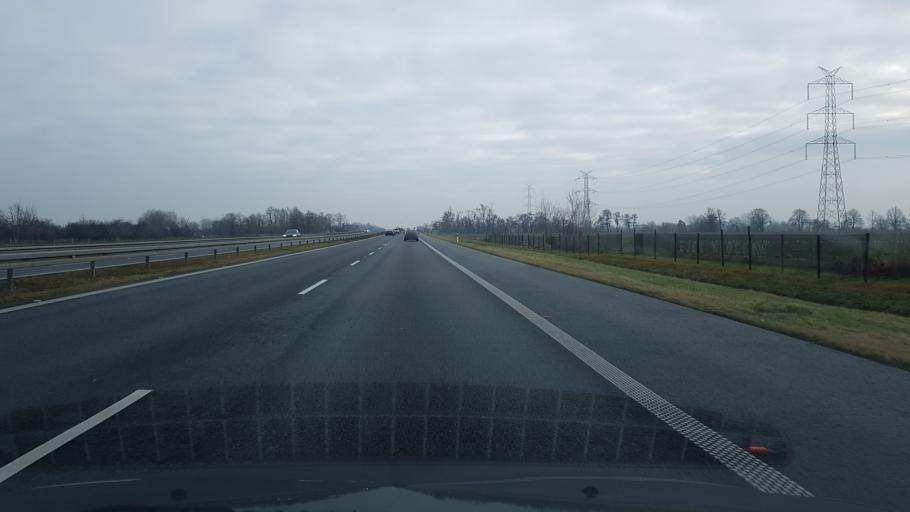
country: PL
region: Lower Silesian Voivodeship
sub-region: Powiat strzelinski
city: Wiazow
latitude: 50.8300
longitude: 17.2898
